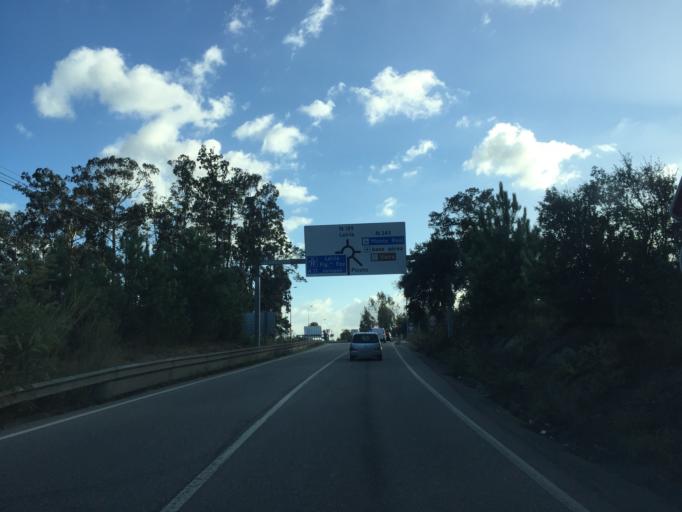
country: PT
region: Leiria
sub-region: Leiria
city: Souto da Carpalhosa
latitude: 39.8557
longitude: -8.8354
